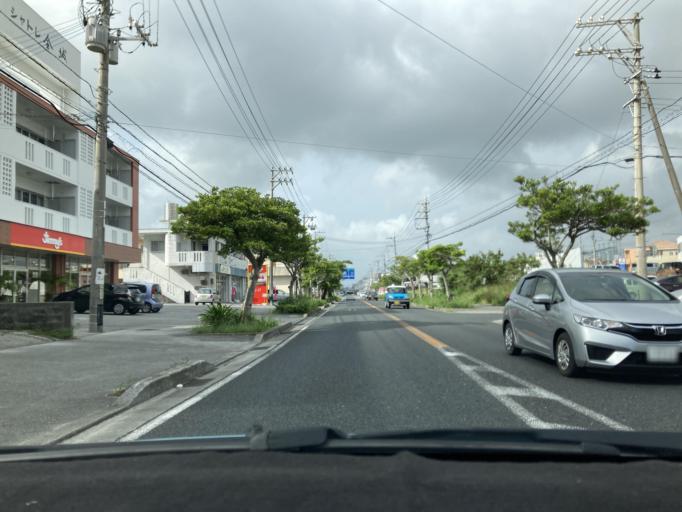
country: JP
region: Okinawa
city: Itoman
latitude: 26.1470
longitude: 127.6734
